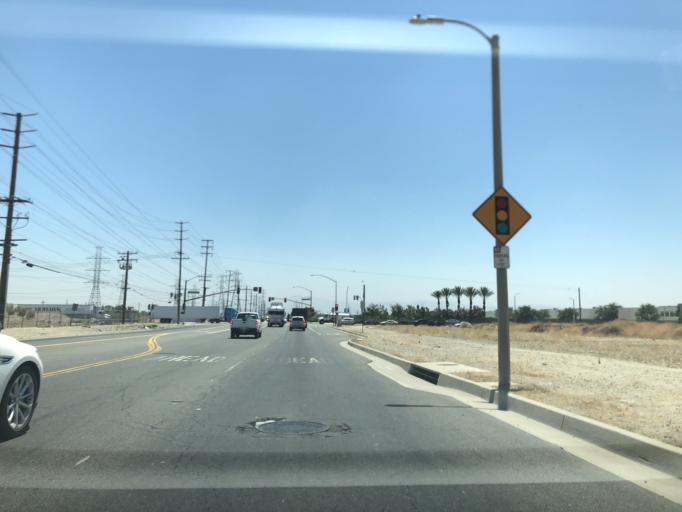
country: US
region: California
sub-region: San Bernardino County
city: Rancho Cucamonga
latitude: 34.0785
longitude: -117.5241
